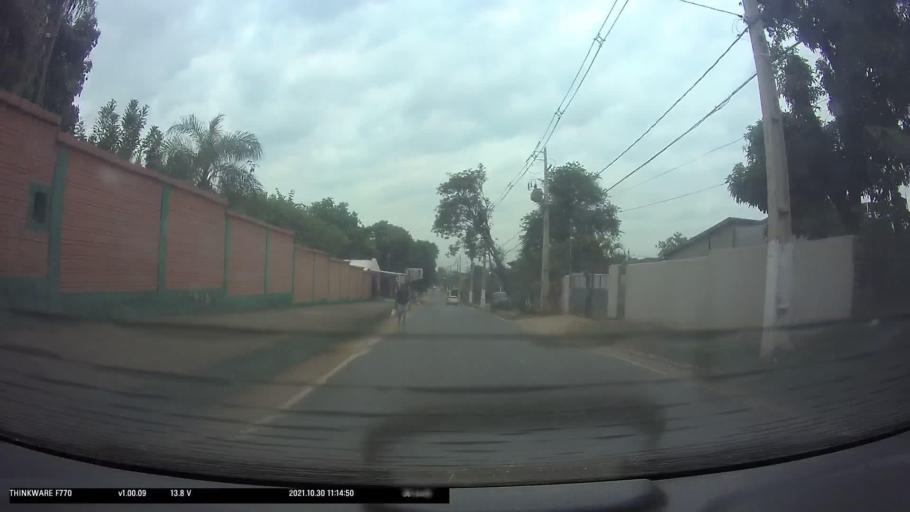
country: PY
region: Central
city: San Lorenzo
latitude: -25.3127
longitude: -57.5126
